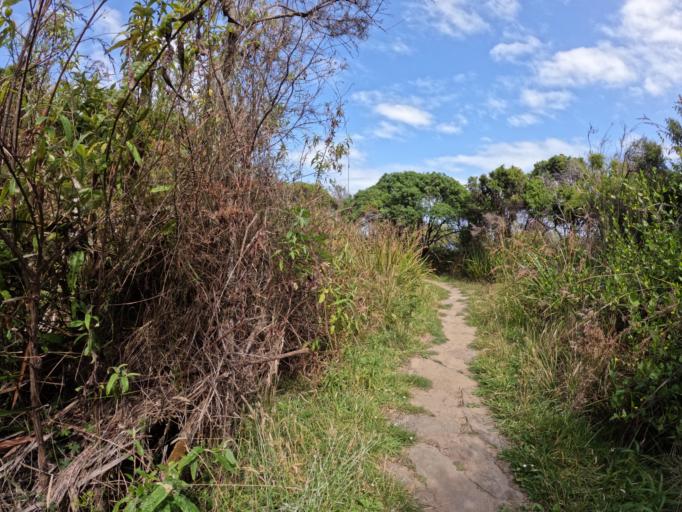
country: AU
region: Victoria
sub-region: Colac-Otway
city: Apollo Bay
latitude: -38.7918
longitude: 143.6228
